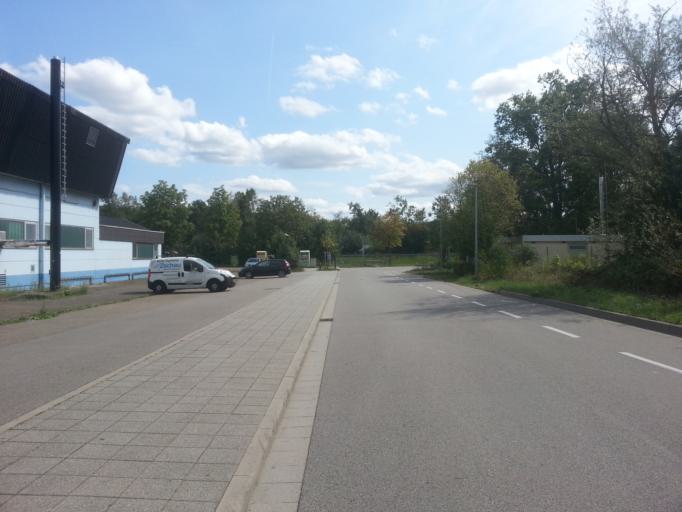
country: DE
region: Hesse
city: Viernheim
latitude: 49.5399
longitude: 8.5951
